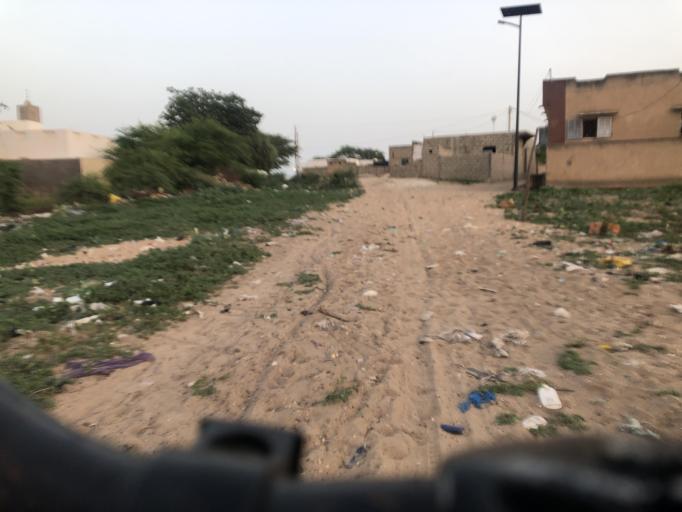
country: SN
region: Saint-Louis
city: Saint-Louis
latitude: 16.0705
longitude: -16.4285
